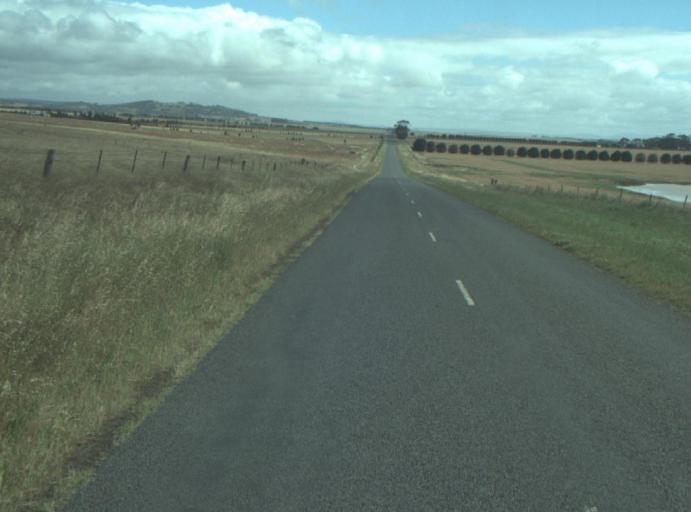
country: AU
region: Victoria
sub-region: Greater Geelong
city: Lara
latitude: -37.9361
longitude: 144.3106
